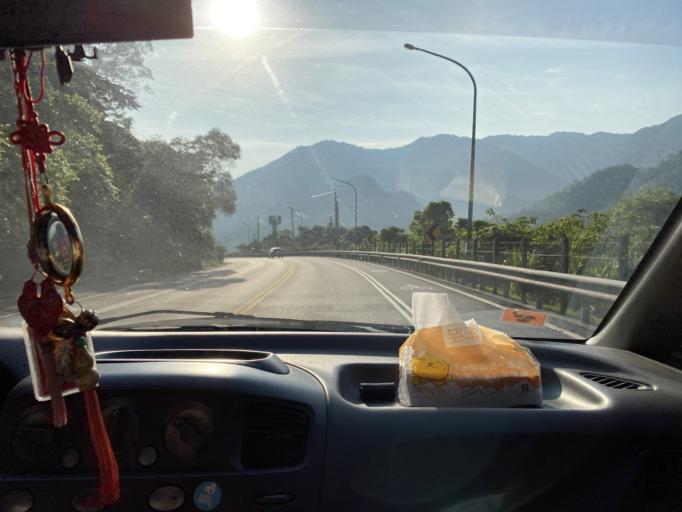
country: TW
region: Taiwan
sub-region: Keelung
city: Keelung
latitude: 25.0166
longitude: 121.7994
